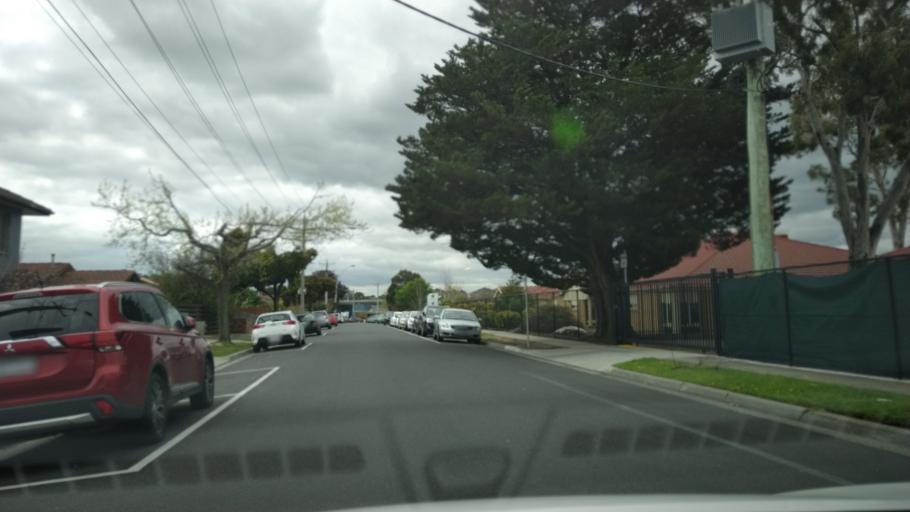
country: AU
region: Victoria
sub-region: Greater Dandenong
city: Noble Park
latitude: -37.9680
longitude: 145.1729
